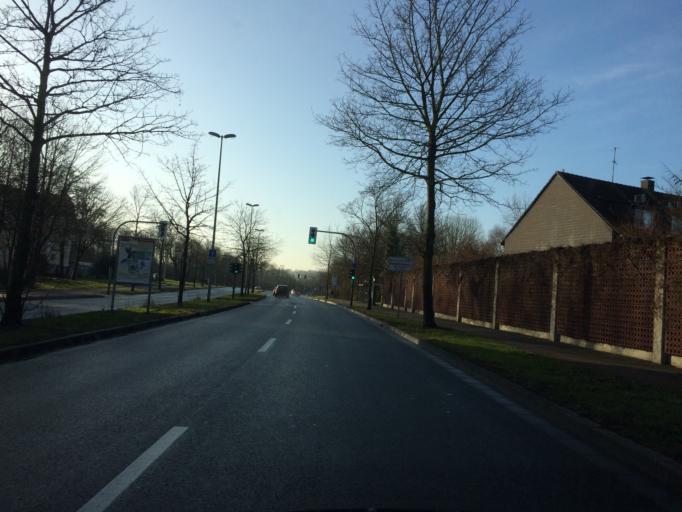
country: DE
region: North Rhine-Westphalia
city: Bochum-Hordel
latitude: 51.5179
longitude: 7.1900
